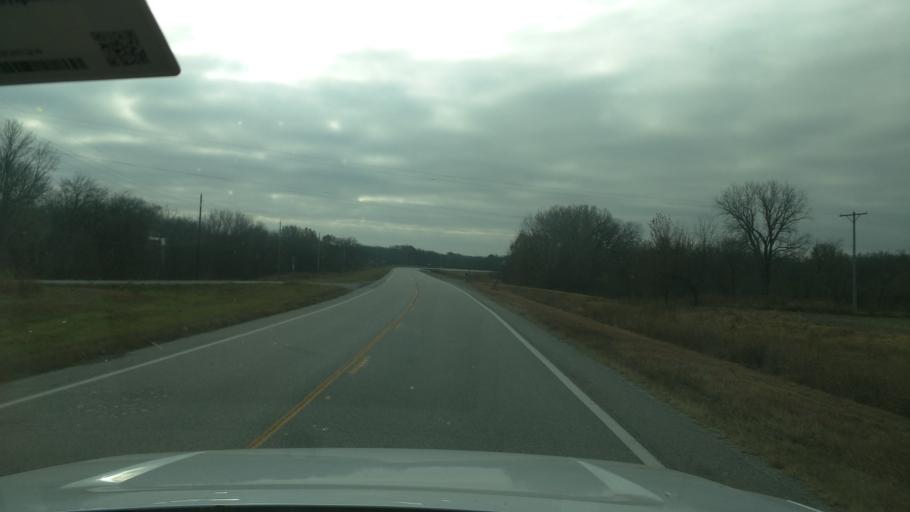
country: US
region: Kansas
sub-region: Greenwood County
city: Eureka
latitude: 37.7114
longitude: -96.2261
